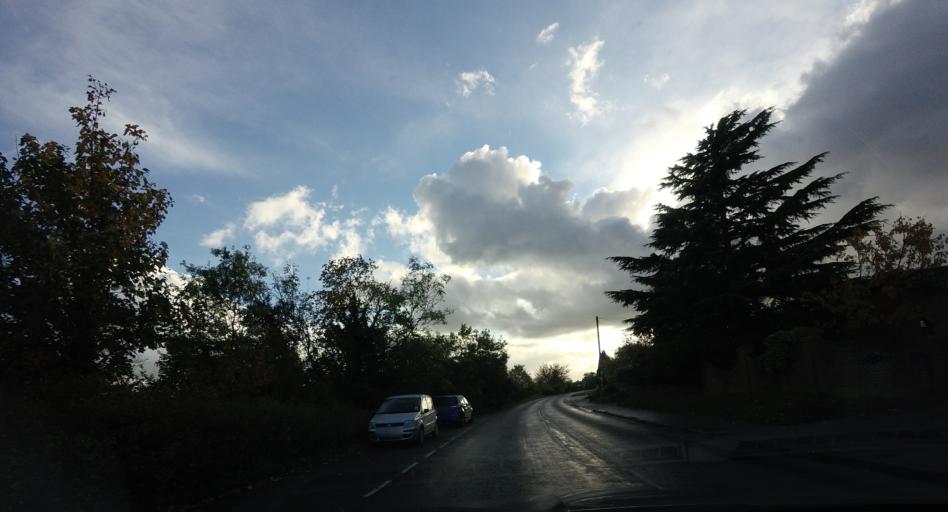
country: GB
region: England
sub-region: Kent
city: Swanley
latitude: 51.4219
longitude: 0.1745
